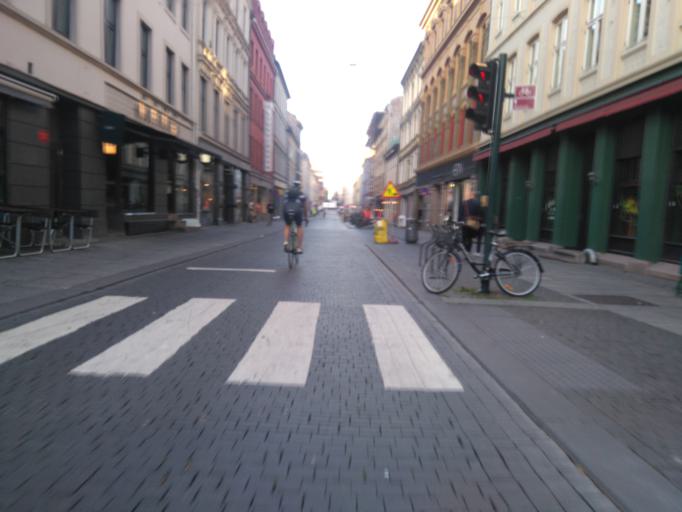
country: NO
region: Oslo
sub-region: Oslo
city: Oslo
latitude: 59.9175
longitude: 10.7543
